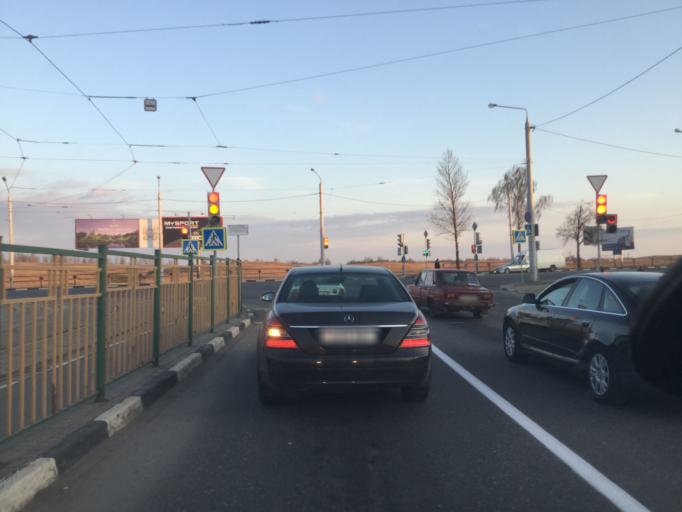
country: BY
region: Vitebsk
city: Vitebsk
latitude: 55.1601
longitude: 30.1696
